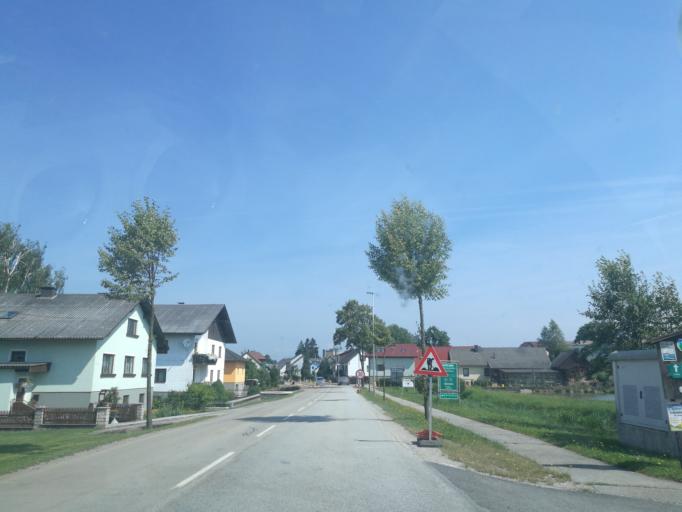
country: AT
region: Lower Austria
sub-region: Politischer Bezirk Gmund
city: Eisgarn
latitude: 48.9128
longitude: 15.1060
